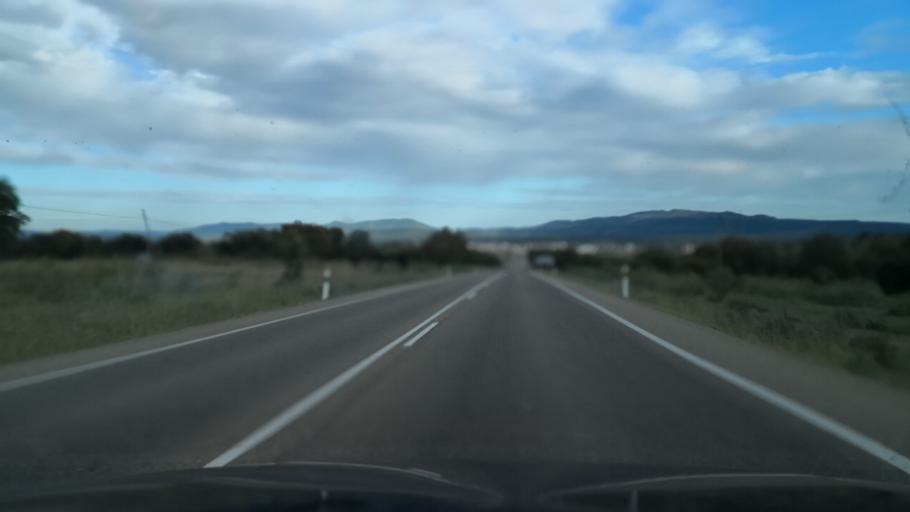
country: ES
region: Extremadura
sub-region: Provincia de Caceres
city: Torrejoncillo
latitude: 39.9127
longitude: -6.4839
